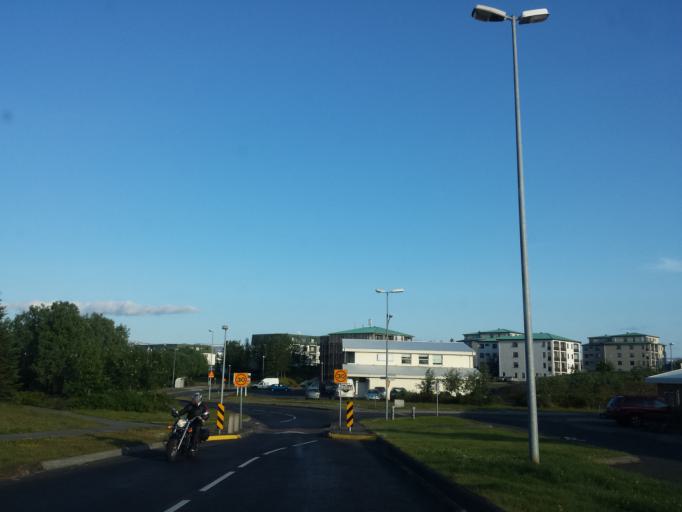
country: IS
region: Capital Region
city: Mosfellsbaer
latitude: 64.1067
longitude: -21.7885
